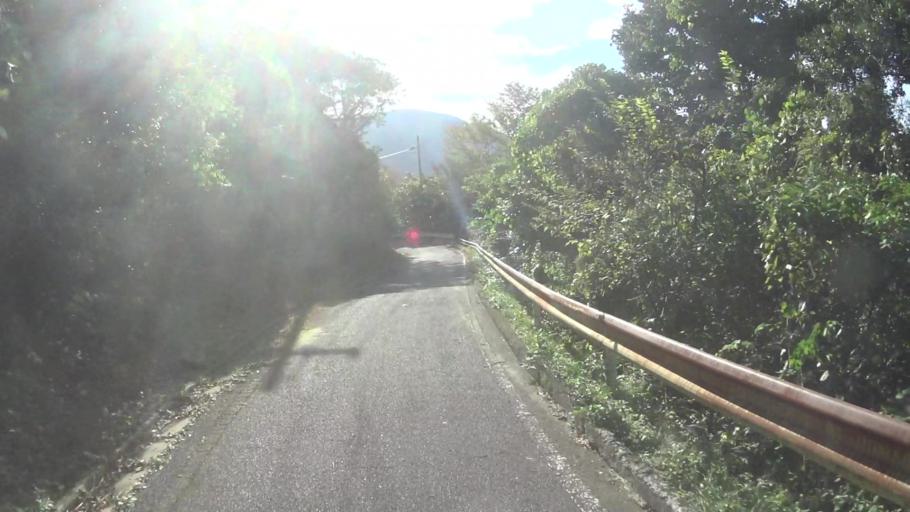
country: JP
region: Kyoto
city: Maizuru
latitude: 35.5651
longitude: 135.4099
